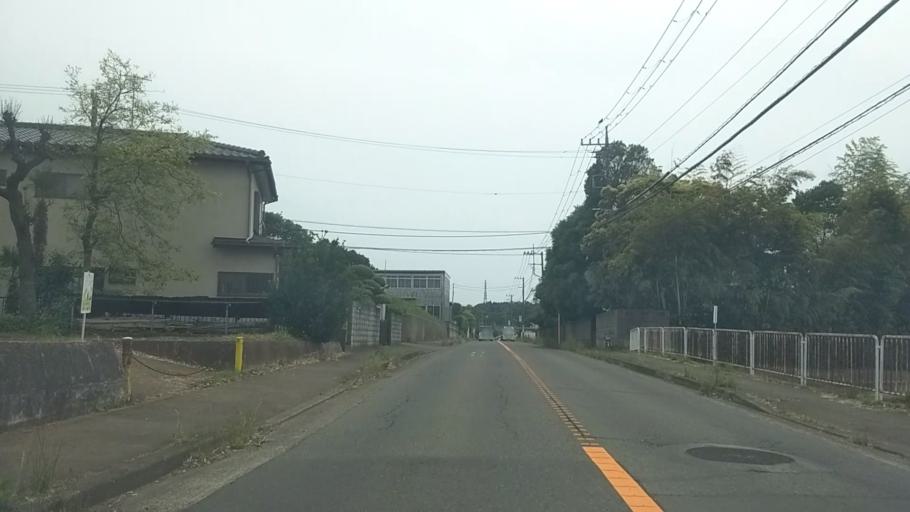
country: JP
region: Kanagawa
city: Chigasaki
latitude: 35.3646
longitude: 139.4217
